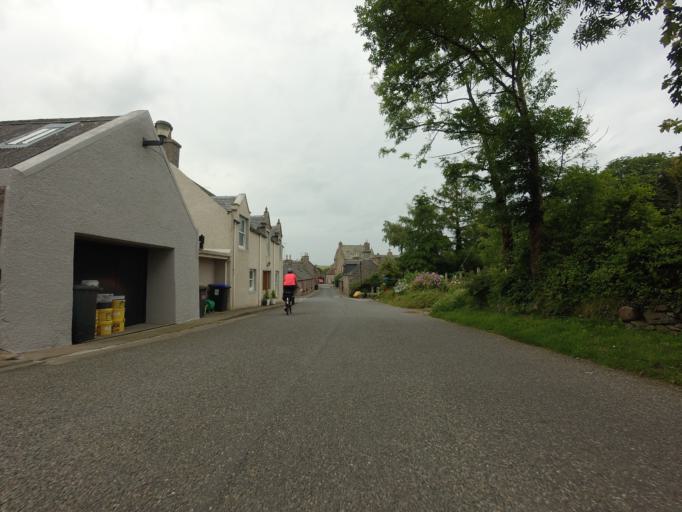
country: GB
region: Scotland
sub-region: Aberdeenshire
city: Portsoy
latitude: 57.6617
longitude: -2.7450
